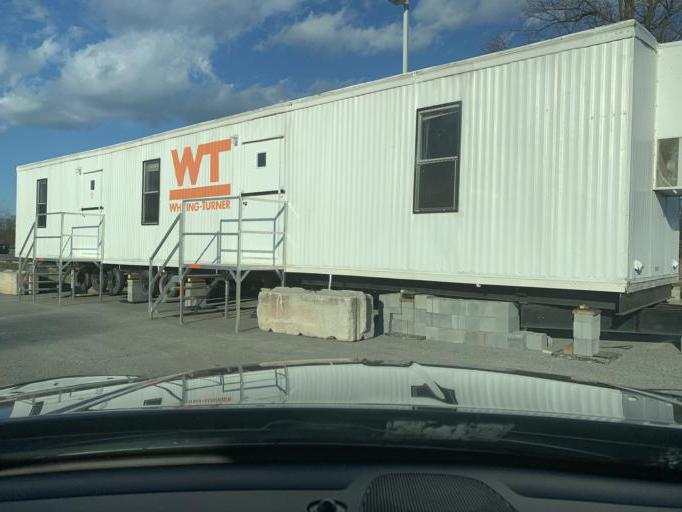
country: US
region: Maryland
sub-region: Anne Arundel County
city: Cape Saint Claire
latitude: 39.0120
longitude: -76.3981
